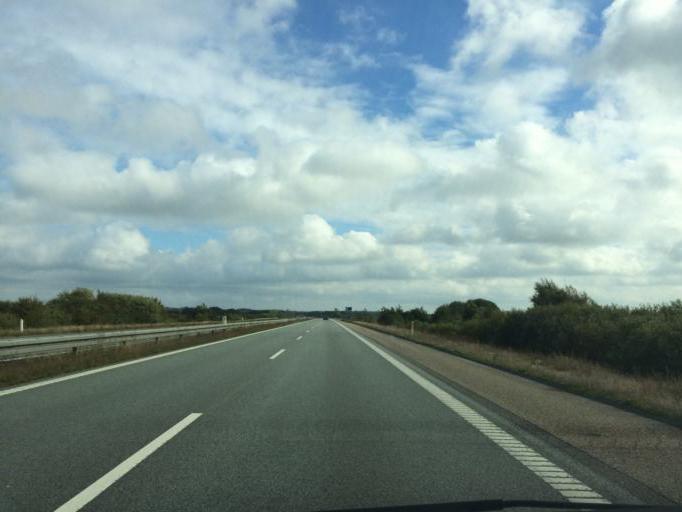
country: DK
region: North Denmark
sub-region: Bronderslev Kommune
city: Hjallerup
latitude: 57.1486
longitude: 10.1297
